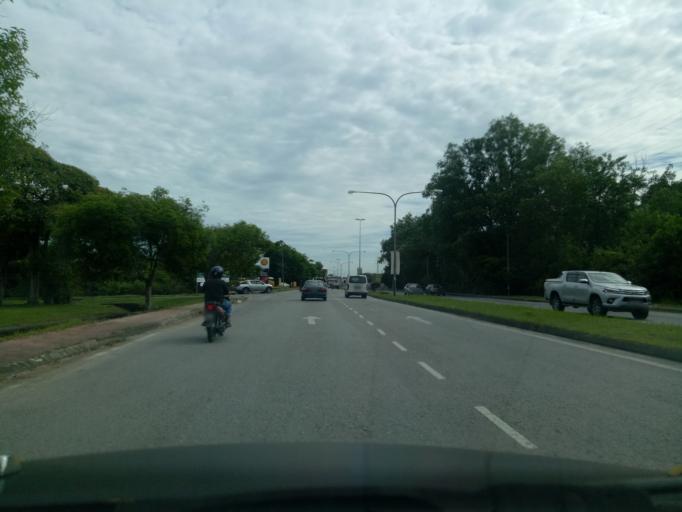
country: MY
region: Sarawak
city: Kuching
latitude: 1.4867
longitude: 110.3309
